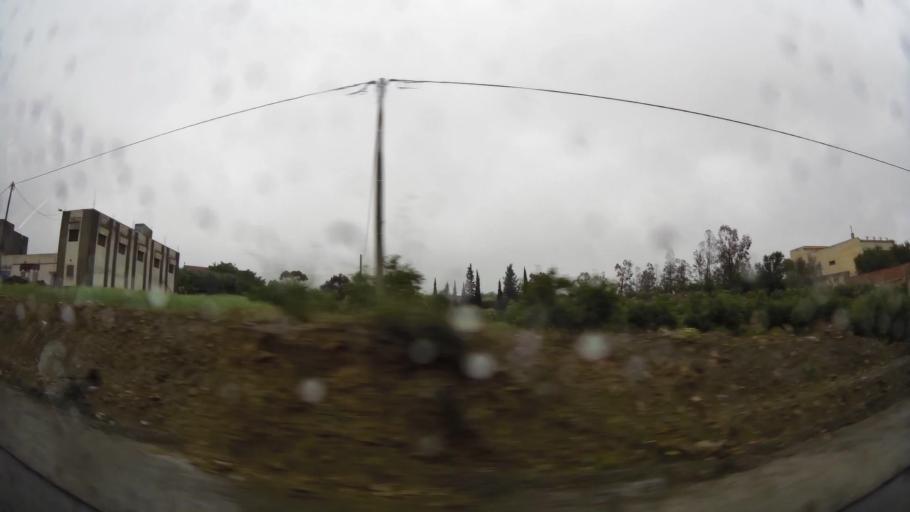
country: MA
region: Taza-Al Hoceima-Taounate
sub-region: Taza
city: Aknoul
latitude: 34.8002
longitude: -3.7414
